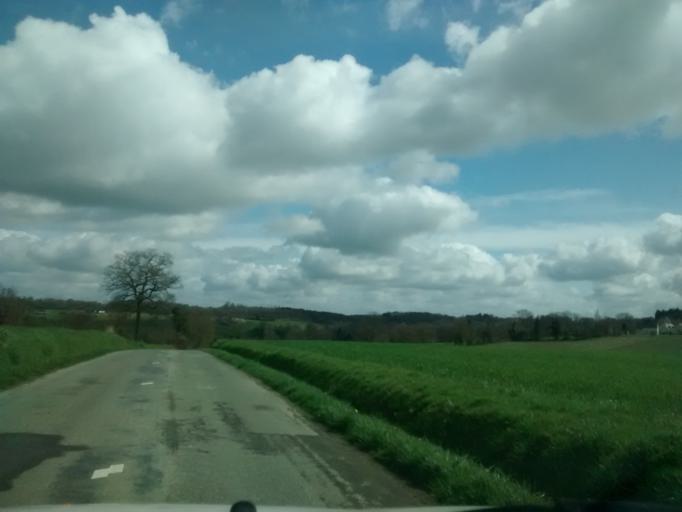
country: FR
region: Brittany
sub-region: Departement d'Ille-et-Vilaine
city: Livre-sur-Changeon
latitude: 48.1964
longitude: -1.3676
